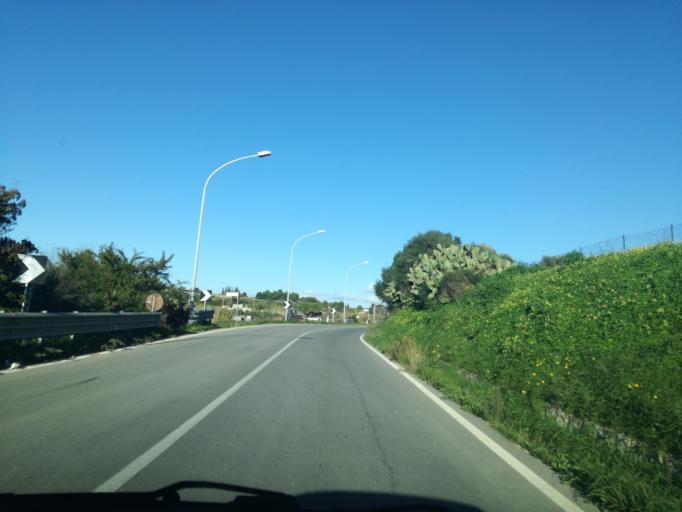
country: IT
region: Sicily
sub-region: Provincia di Caltanissetta
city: Gela
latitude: 37.1039
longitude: 14.1581
